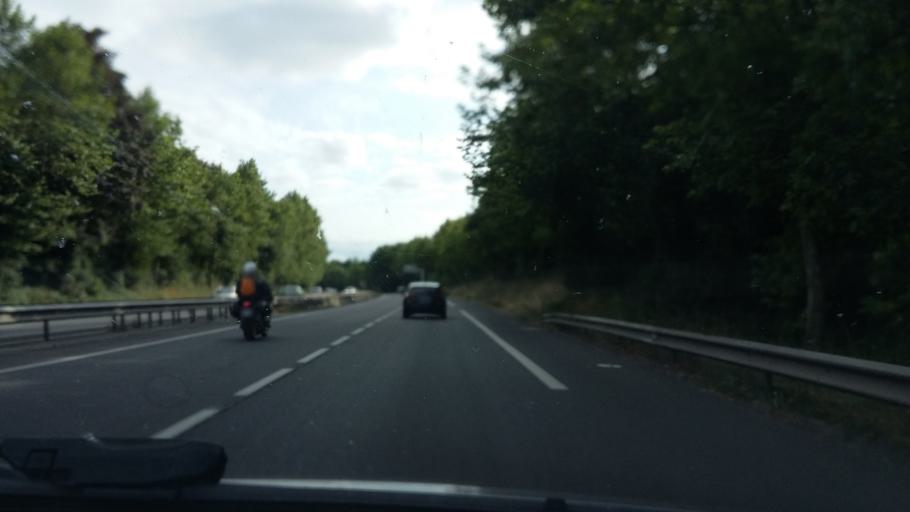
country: FR
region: Poitou-Charentes
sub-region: Departement de la Charente
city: Saint-Michel
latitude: 45.6579
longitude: 0.1226
